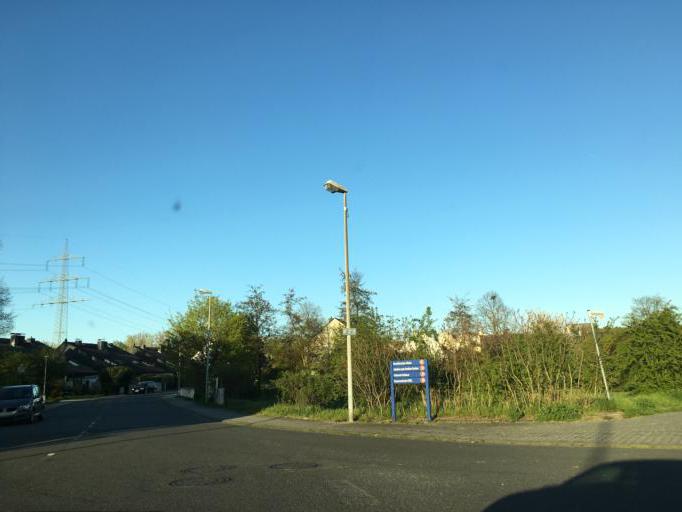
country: DE
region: Hesse
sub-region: Regierungsbezirk Darmstadt
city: Rodgau
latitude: 50.0143
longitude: 8.8908
